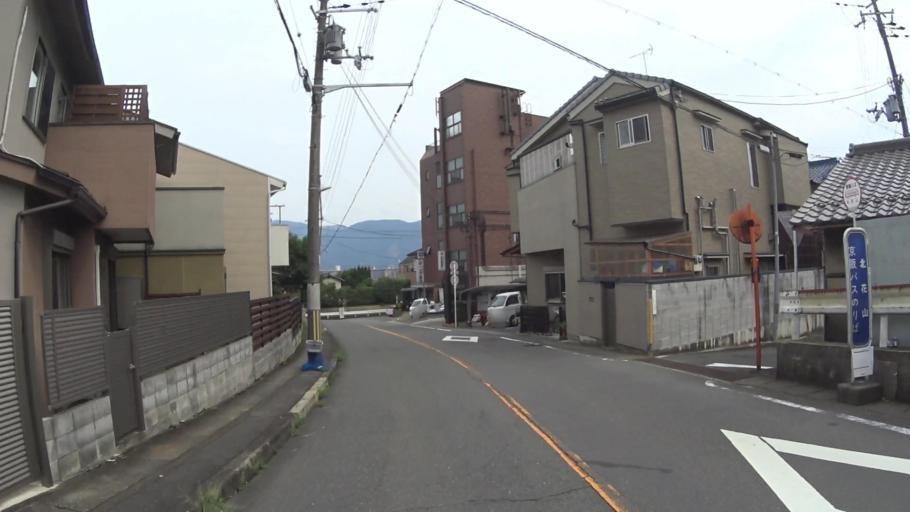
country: JP
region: Kyoto
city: Kyoto
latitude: 34.9890
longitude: 135.7985
